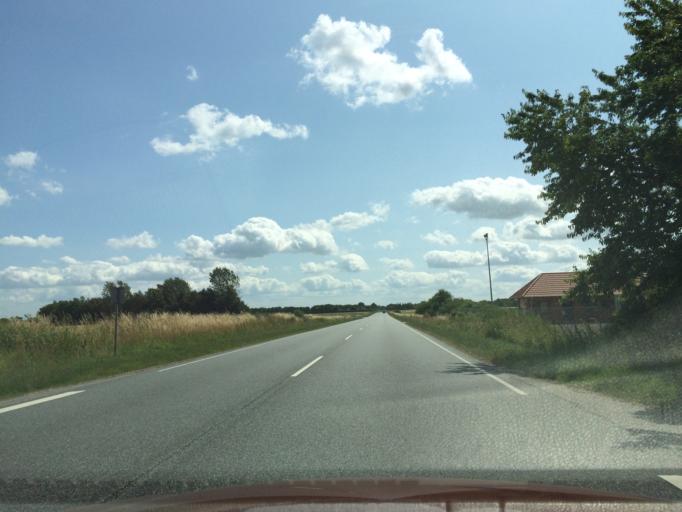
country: DK
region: Central Jutland
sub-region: Favrskov Kommune
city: Hammel
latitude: 56.2613
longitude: 9.7478
